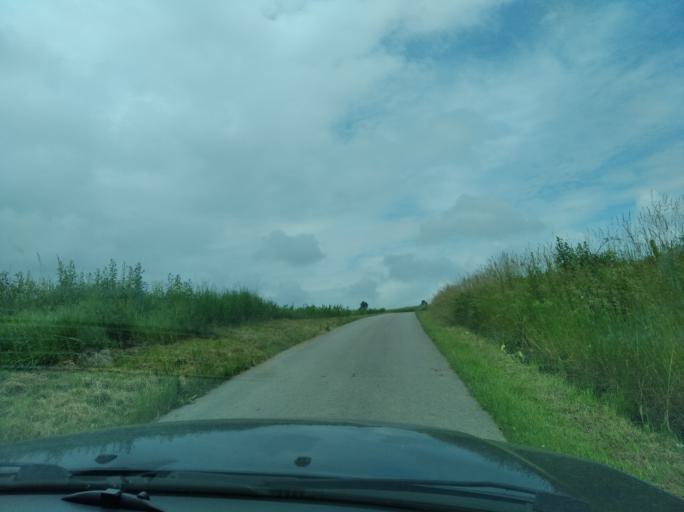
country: PL
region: Subcarpathian Voivodeship
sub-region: Powiat jaroslawski
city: Pruchnik
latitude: 49.9036
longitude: 22.4993
